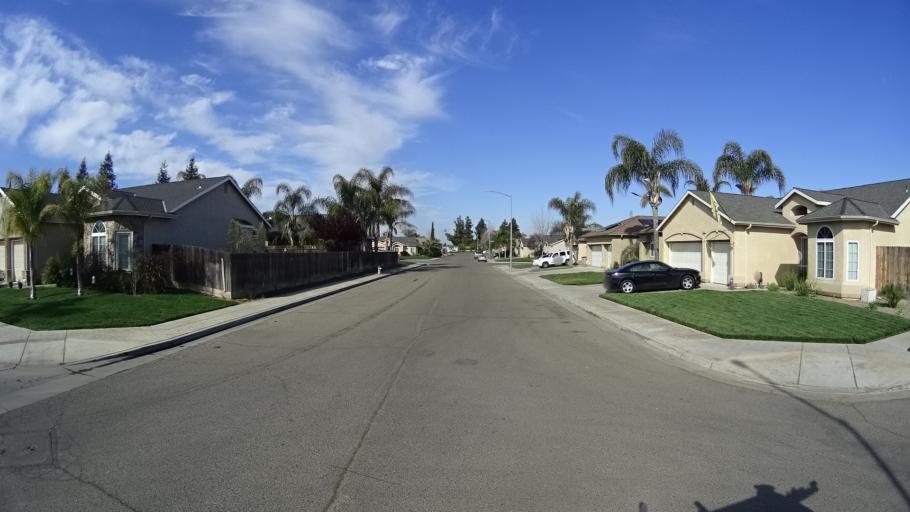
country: US
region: California
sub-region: Fresno County
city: West Park
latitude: 36.8023
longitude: -119.8958
